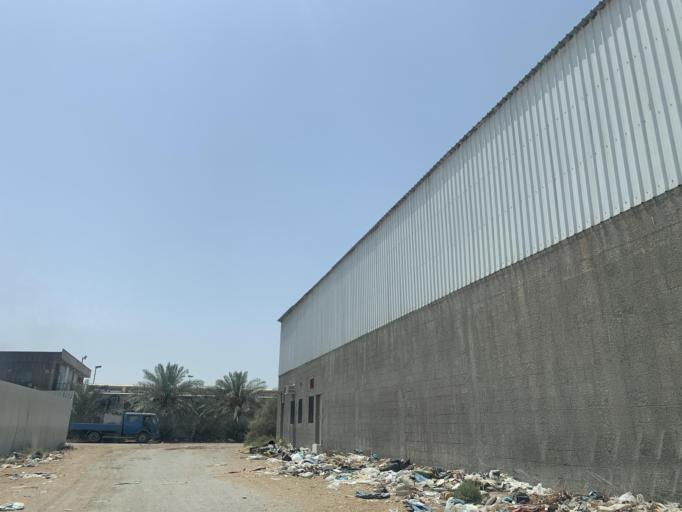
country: BH
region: Central Governorate
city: Madinat Hamad
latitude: 26.1620
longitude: 50.4932
